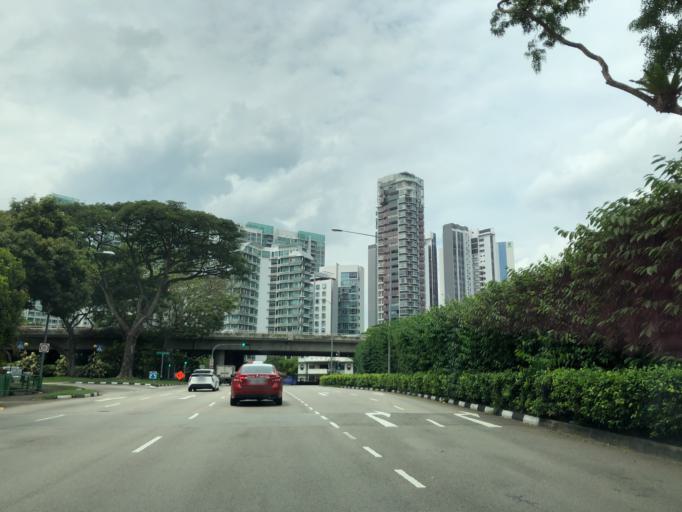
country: SG
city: Singapore
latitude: 1.3128
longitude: 103.8462
